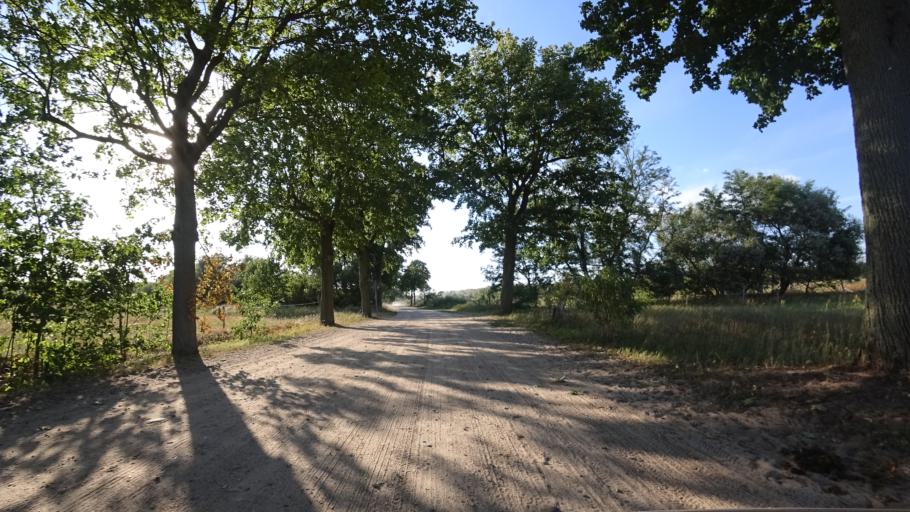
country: DE
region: Brandenburg
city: Stahnsdorf
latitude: 52.3438
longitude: 13.1810
